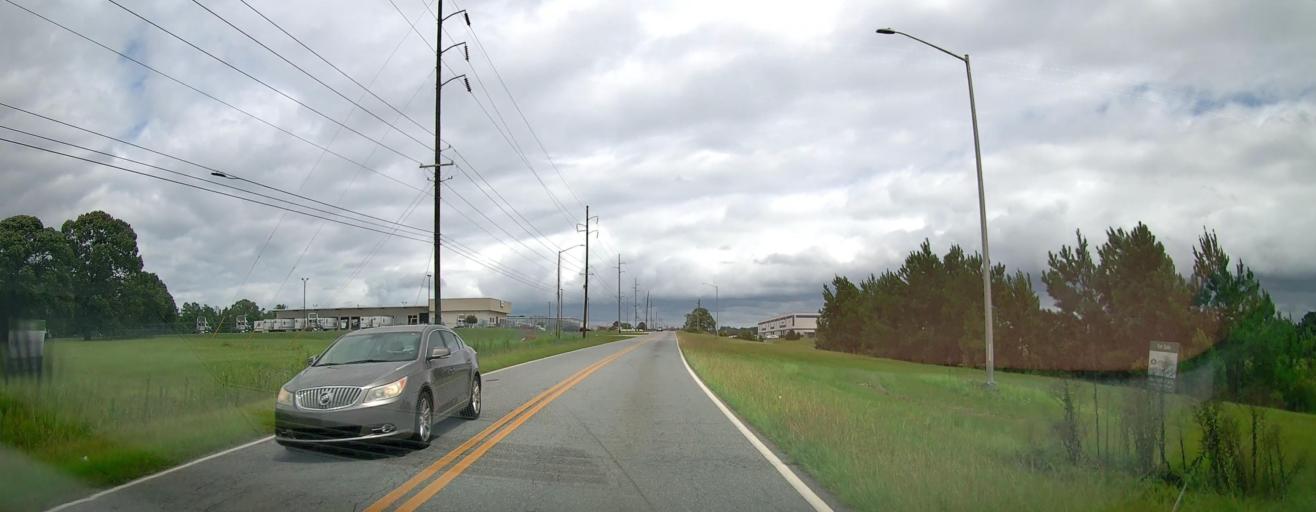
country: US
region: Georgia
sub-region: Bibb County
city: Macon
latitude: 32.8005
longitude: -83.5590
